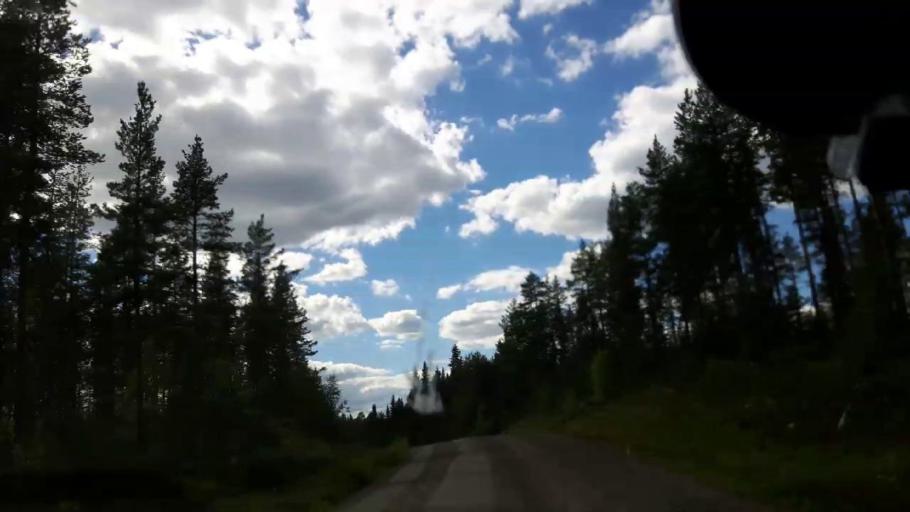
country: SE
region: Vaesternorrland
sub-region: Ange Kommun
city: Ange
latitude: 62.7707
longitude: 15.8868
